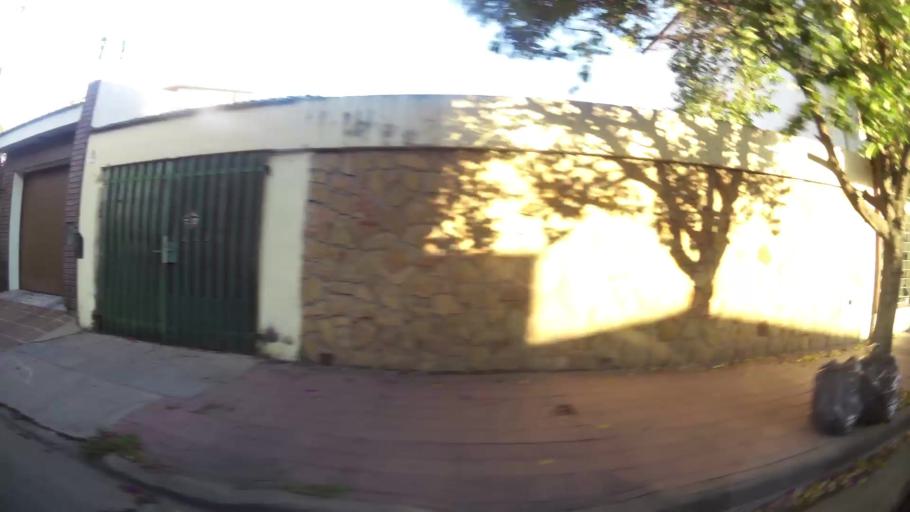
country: AR
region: Cordoba
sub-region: Departamento de Capital
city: Cordoba
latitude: -31.3851
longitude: -64.2172
